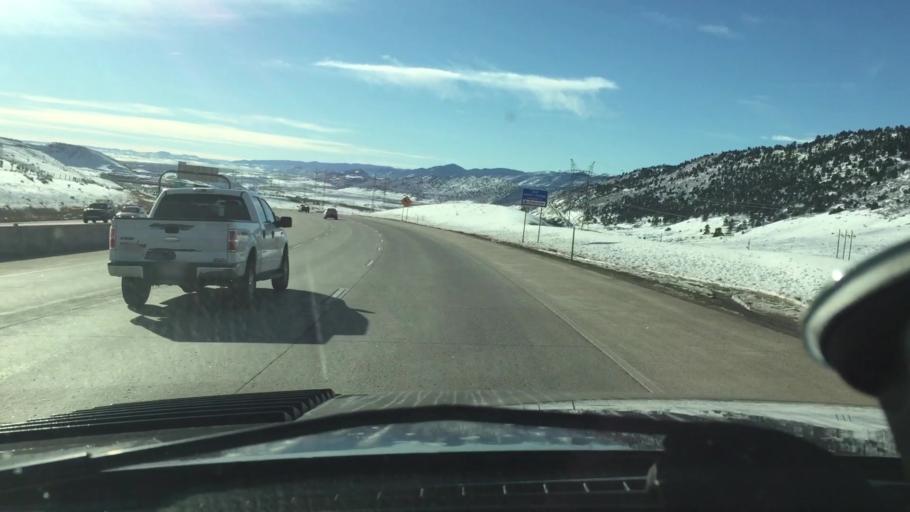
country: US
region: Colorado
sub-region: Jefferson County
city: West Pleasant View
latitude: 39.7005
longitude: -105.1936
